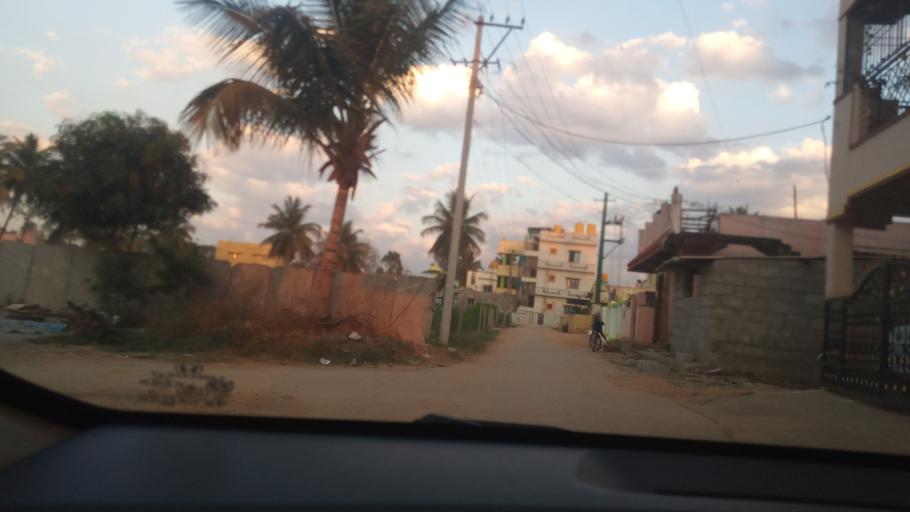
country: IN
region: Karnataka
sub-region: Bangalore Rural
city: Hoskote
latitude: 12.9792
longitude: 77.8005
